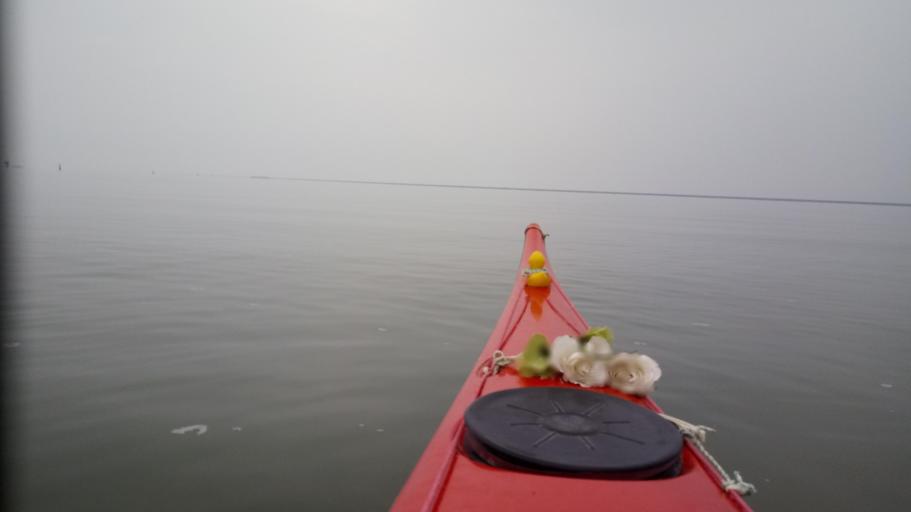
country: NL
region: Flevoland
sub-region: Gemeente Lelystad
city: Lelystad
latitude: 52.5716
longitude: 5.4179
